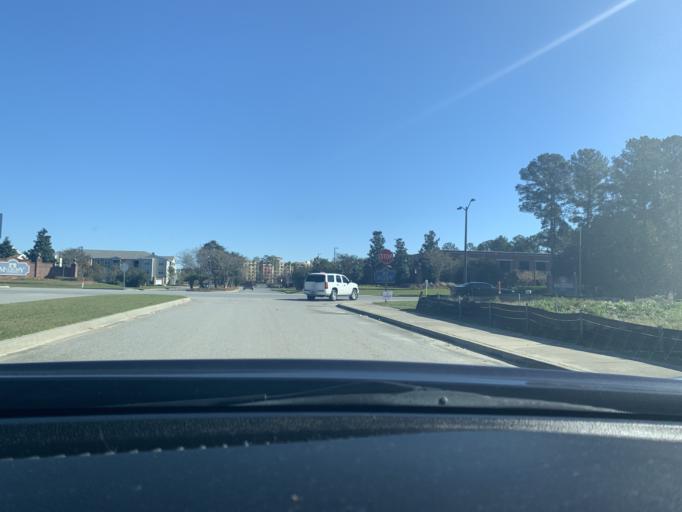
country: US
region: Georgia
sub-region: Chatham County
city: Pooler
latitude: 32.1458
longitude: -81.2481
